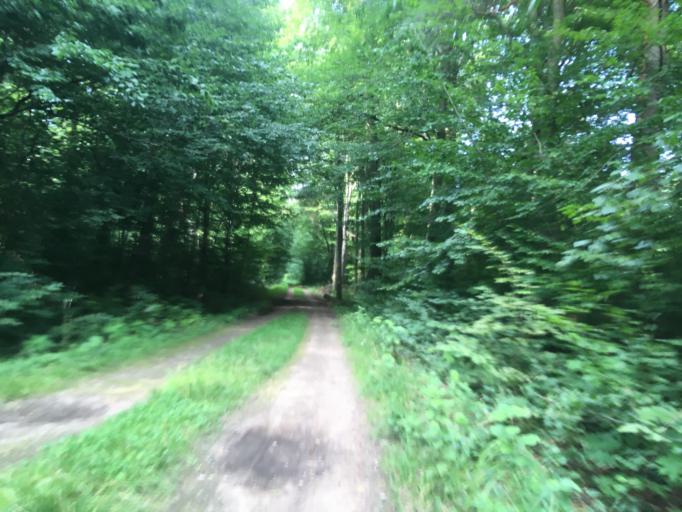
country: DE
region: Brandenburg
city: Eberswalde
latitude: 52.8149
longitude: 13.8188
